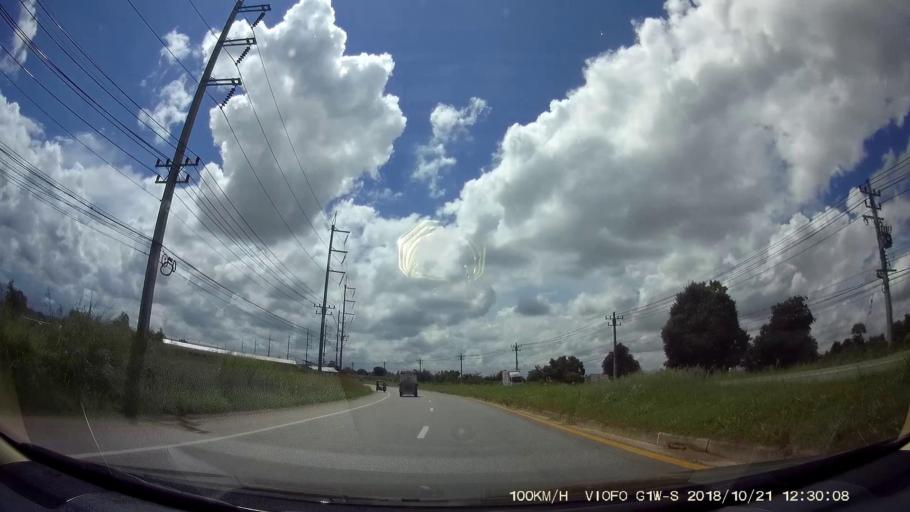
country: TH
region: Nakhon Ratchasima
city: Dan Khun Thot
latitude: 15.1751
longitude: 101.7408
